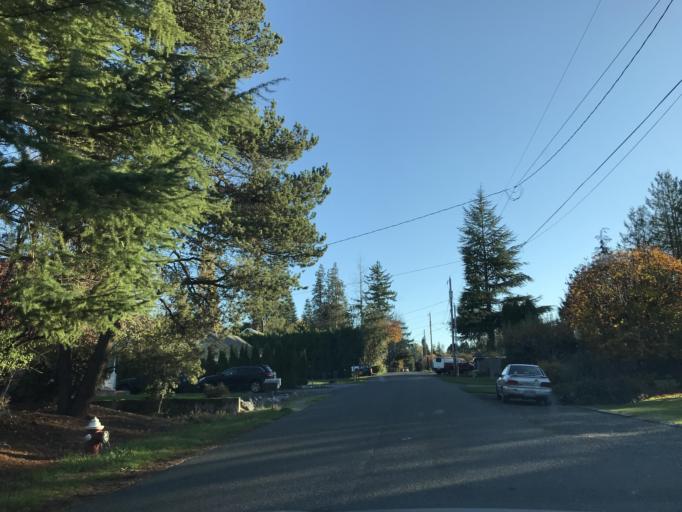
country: US
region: Washington
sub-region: Whatcom County
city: Geneva
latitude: 48.7468
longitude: -122.4306
